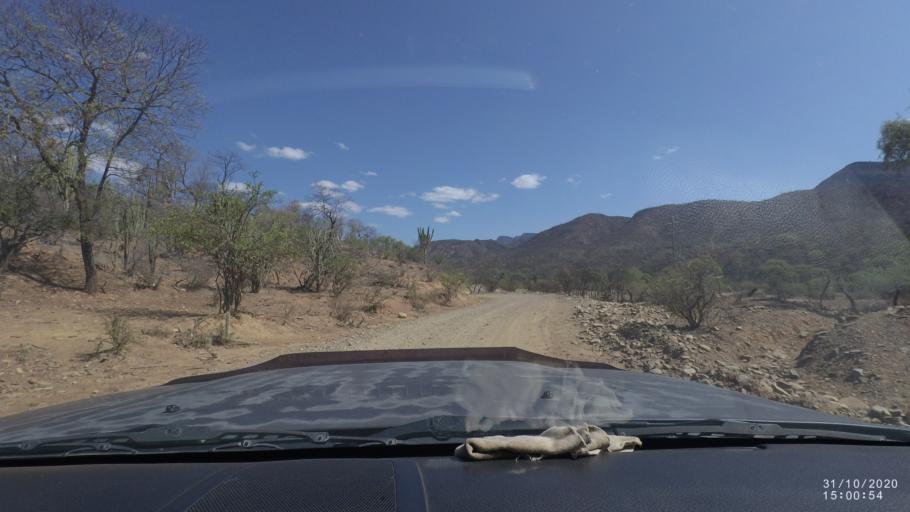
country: BO
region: Cochabamba
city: Aiquile
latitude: -18.2601
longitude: -64.8219
